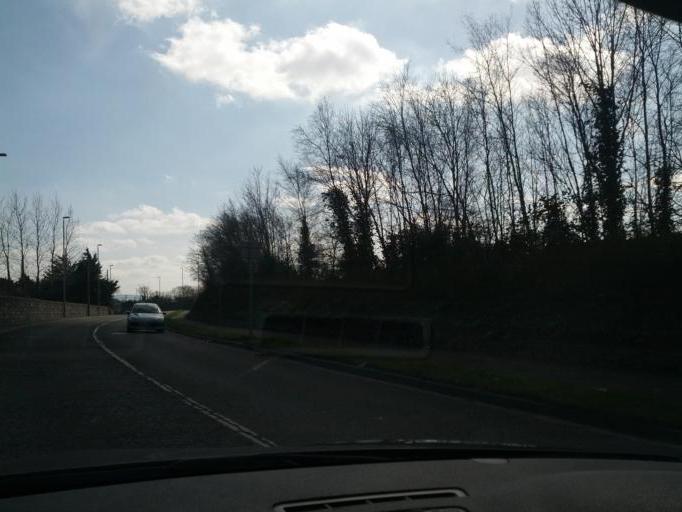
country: IE
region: Leinster
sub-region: Kildare
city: Leixlip
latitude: 53.3469
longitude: -6.5082
